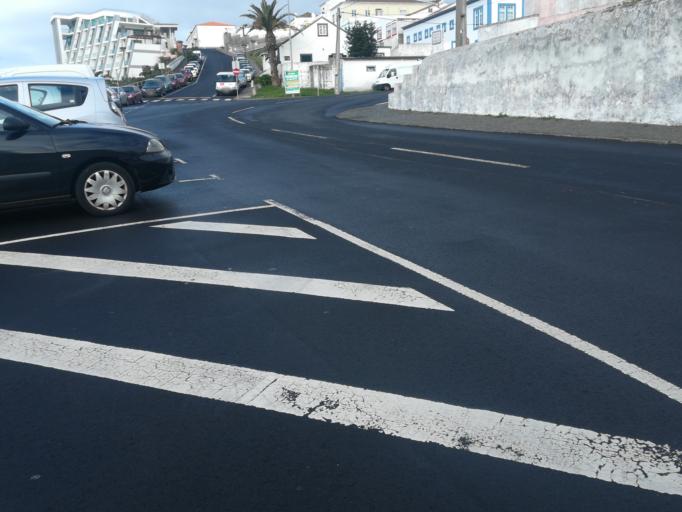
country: PT
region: Azores
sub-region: Angra do Heroismo
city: Angra do Heroismo
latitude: 38.6526
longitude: -27.2130
